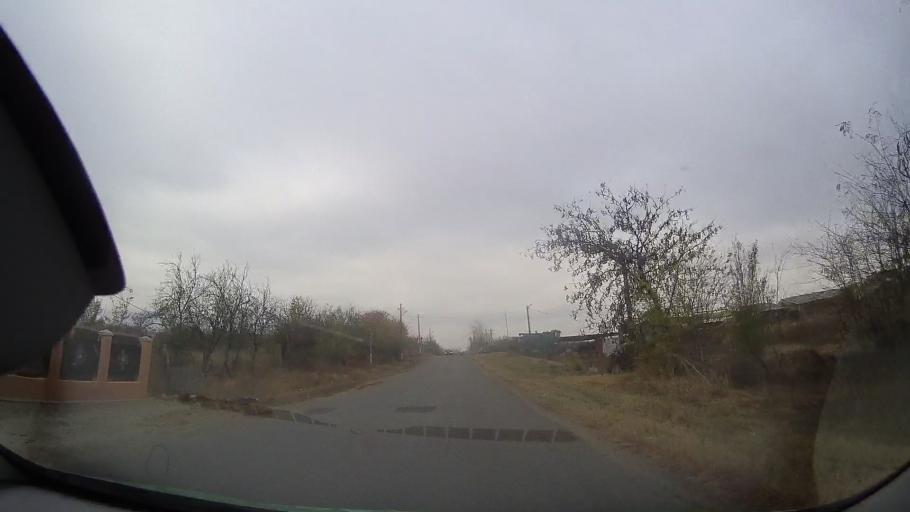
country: RO
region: Buzau
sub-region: Comuna Largu
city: Largu
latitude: 44.9743
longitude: 27.1537
